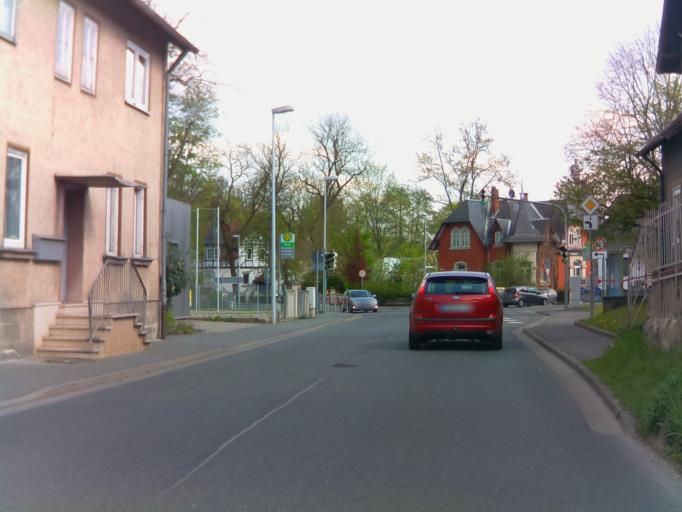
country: DE
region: Bavaria
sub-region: Upper Franconia
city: Coburg
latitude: 50.2744
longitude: 10.9474
